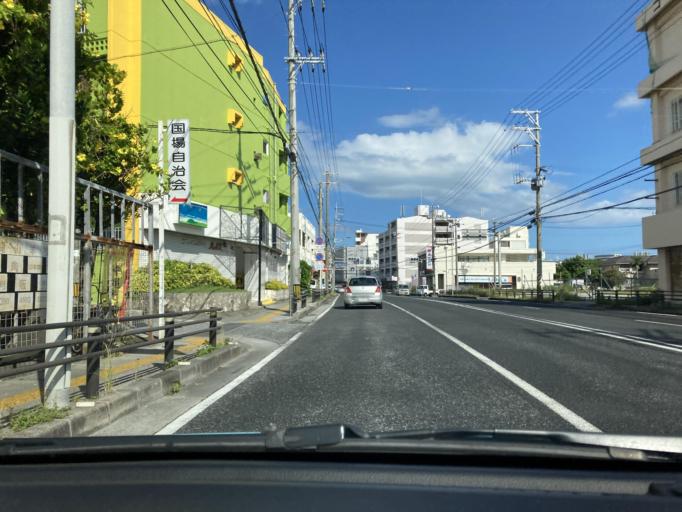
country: JP
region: Okinawa
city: Tomigusuku
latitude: 26.1957
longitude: 127.7021
